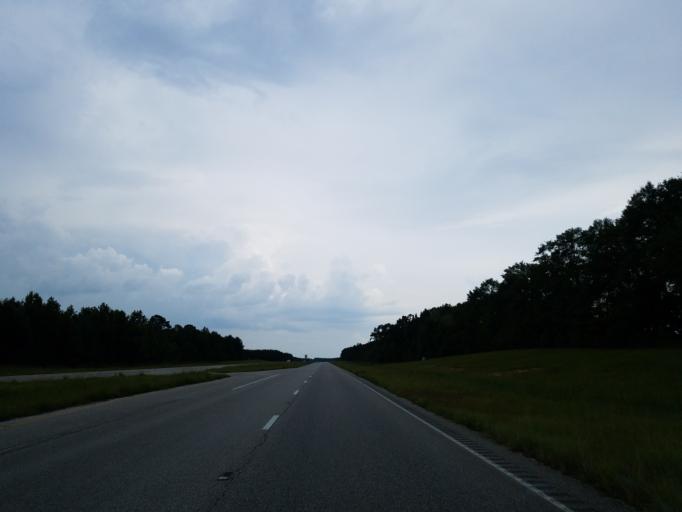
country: US
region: Mississippi
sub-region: Wayne County
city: Belmont
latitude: 31.4273
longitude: -88.4662
